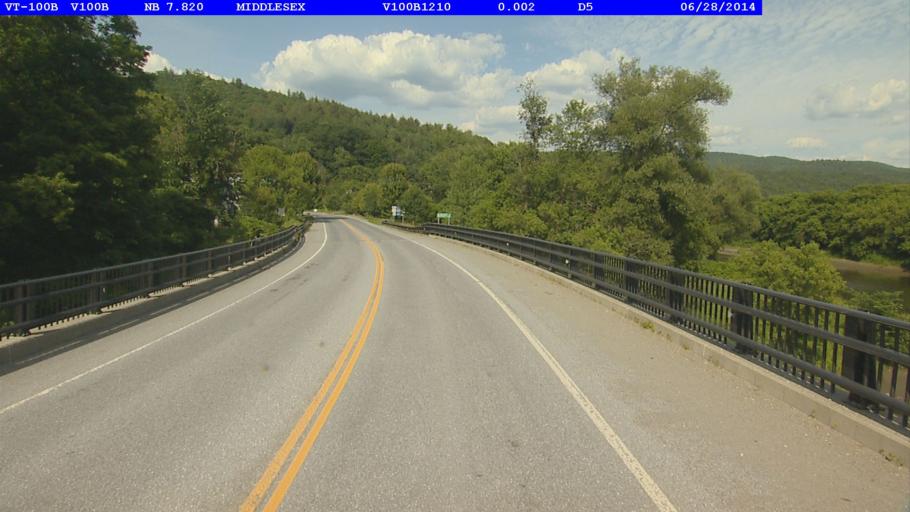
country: US
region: Vermont
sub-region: Washington County
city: Waterbury
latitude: 44.2911
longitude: -72.6792
